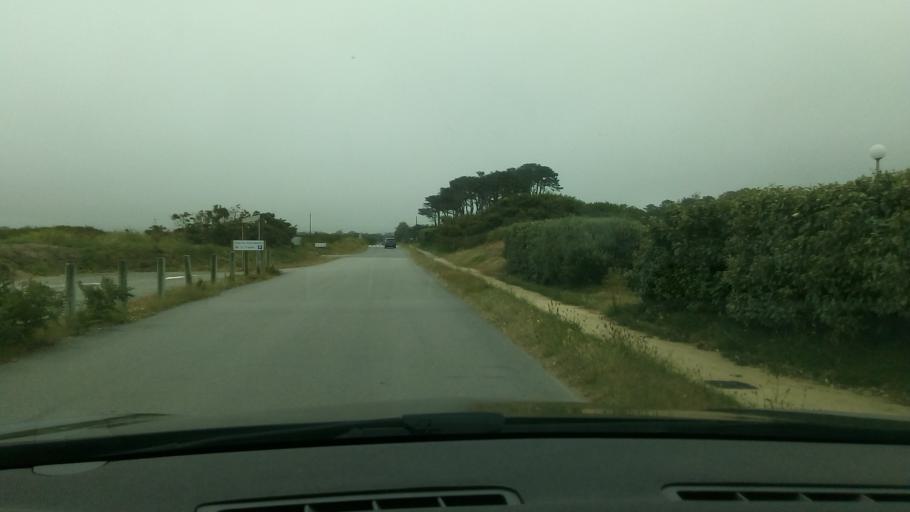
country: FR
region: Brittany
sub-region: Departement du Finistere
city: Le Conquet
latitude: 48.3675
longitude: -4.7597
